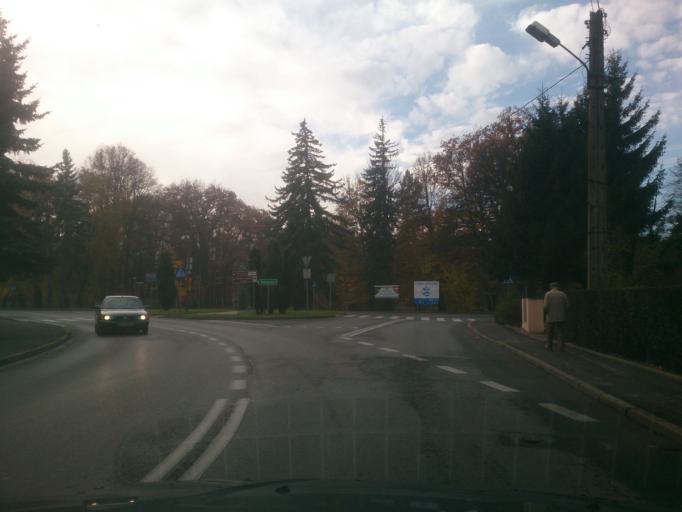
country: PL
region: Lower Silesian Voivodeship
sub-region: Jelenia Gora
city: Cieplice Slaskie Zdroj
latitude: 50.8585
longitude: 15.6825
